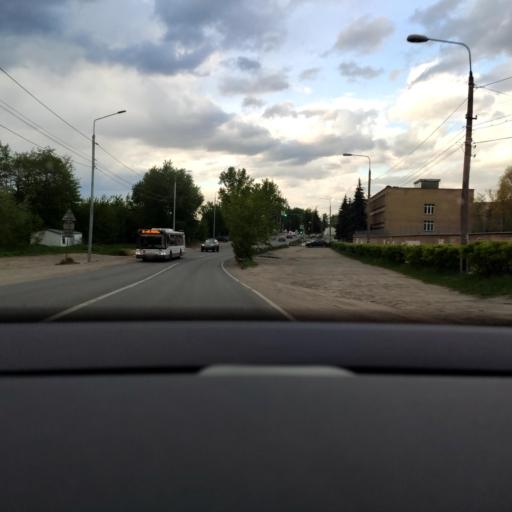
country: RU
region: Moskovskaya
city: Saltykovka
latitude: 55.7356
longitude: 37.9683
